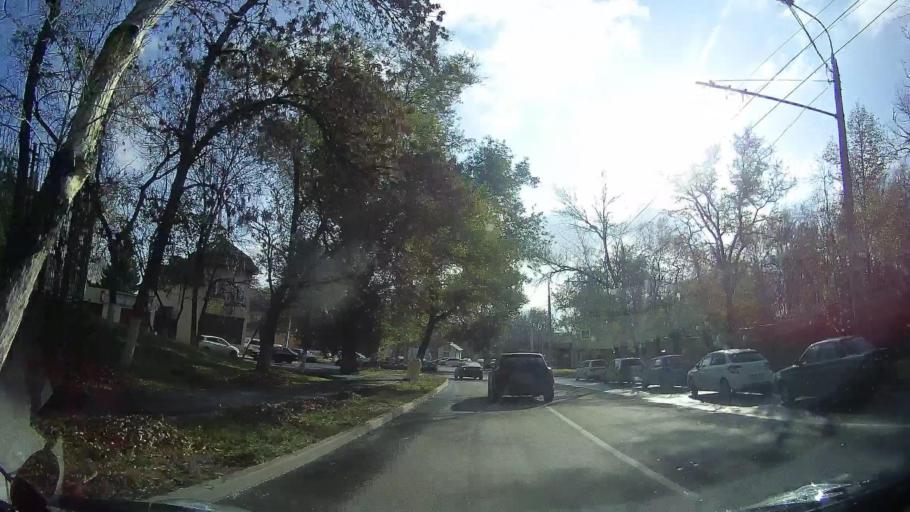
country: RU
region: Rostov
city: Severnyy
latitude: 47.2604
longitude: 39.6741
